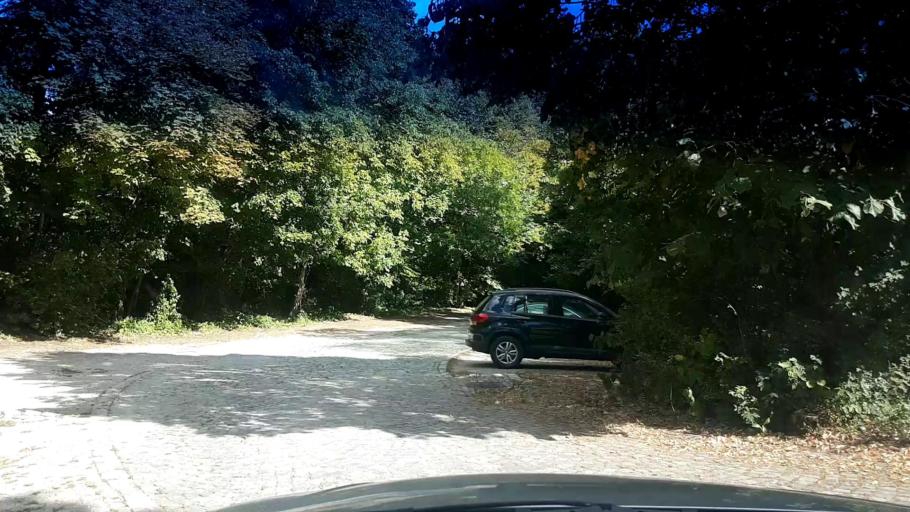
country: DE
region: Bavaria
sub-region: Upper Franconia
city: Schesslitz
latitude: 49.9523
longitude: 11.0618
